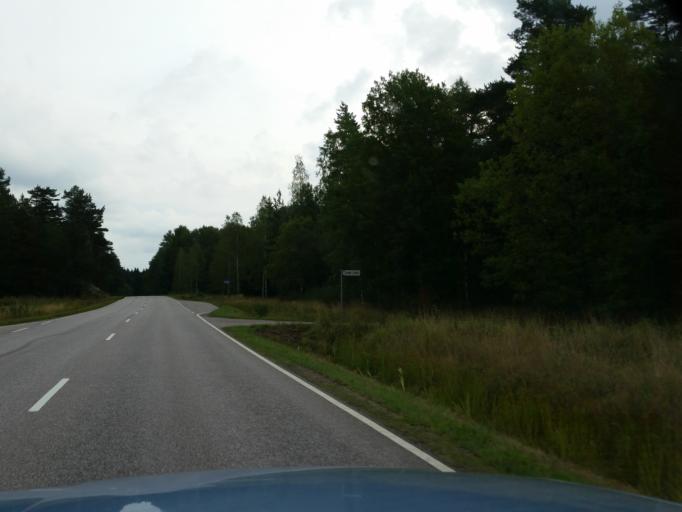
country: FI
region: Varsinais-Suomi
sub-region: Aboland-Turunmaa
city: Nagu
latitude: 60.2103
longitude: 22.0668
